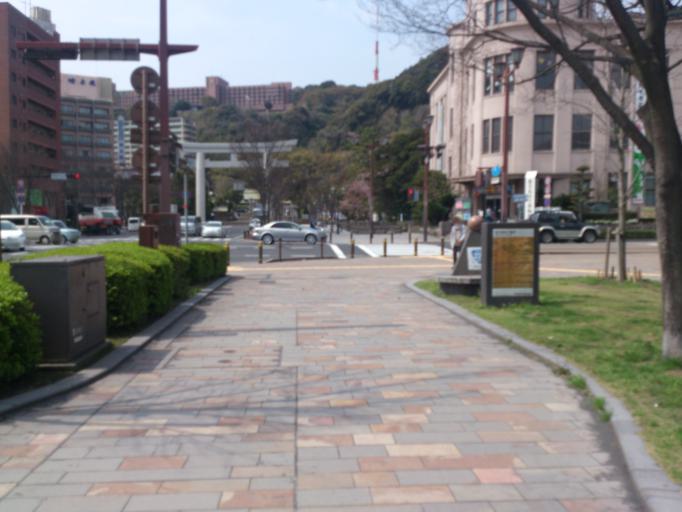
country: JP
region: Kagoshima
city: Kagoshima-shi
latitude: 31.5935
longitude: 130.5531
